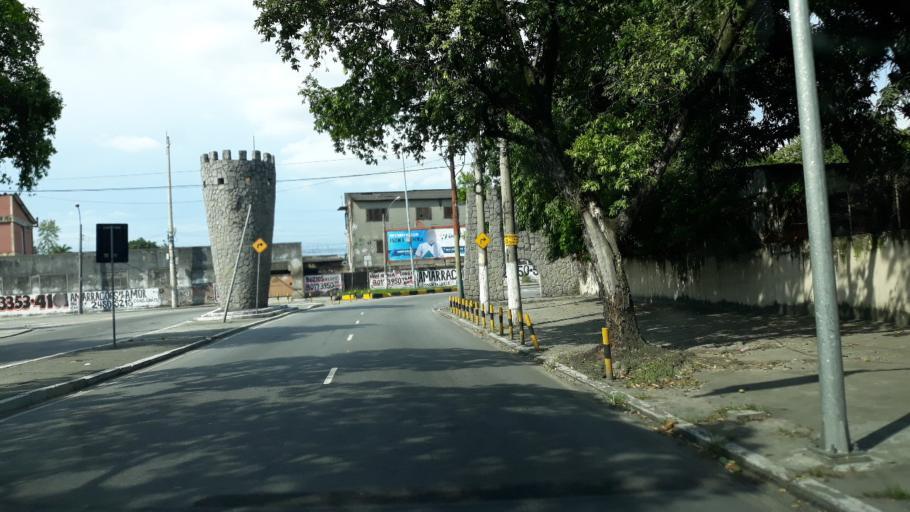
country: BR
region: Rio de Janeiro
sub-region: Sao Joao De Meriti
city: Sao Joao de Meriti
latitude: -22.8554
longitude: -43.3856
